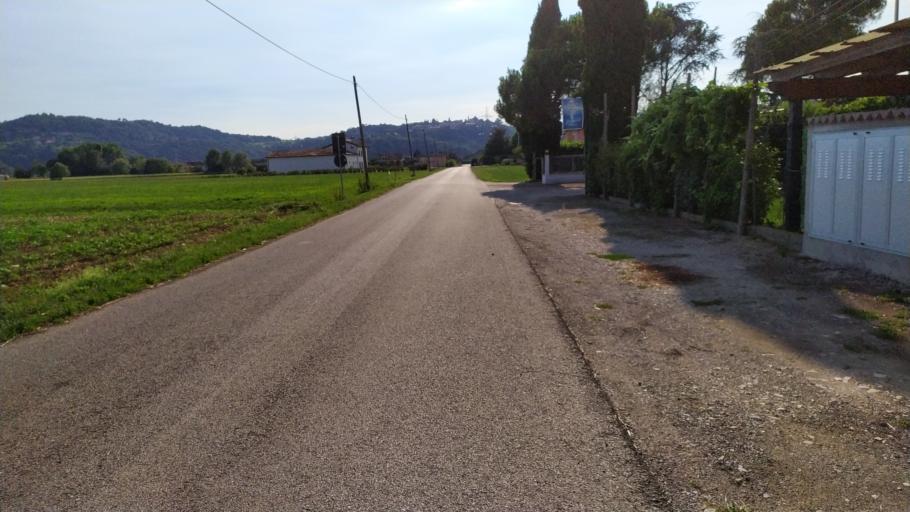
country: IT
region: Veneto
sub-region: Provincia di Vicenza
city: Costabissara
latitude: 45.5640
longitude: 11.4868
